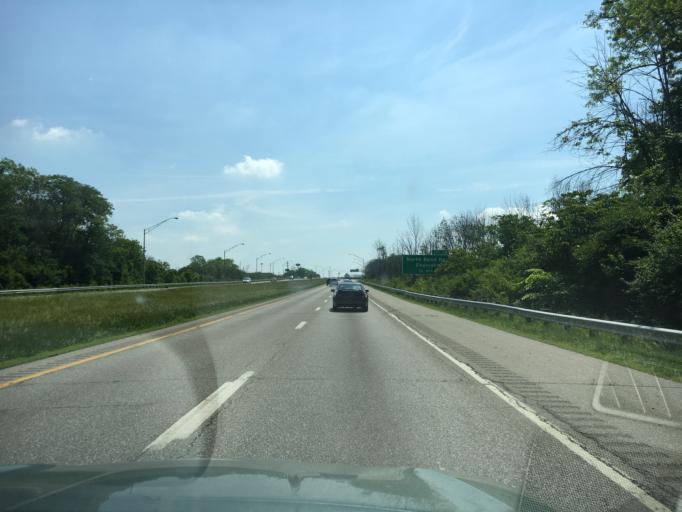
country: US
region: Ohio
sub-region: Hamilton County
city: Monfort Heights
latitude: 39.1858
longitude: -84.6142
